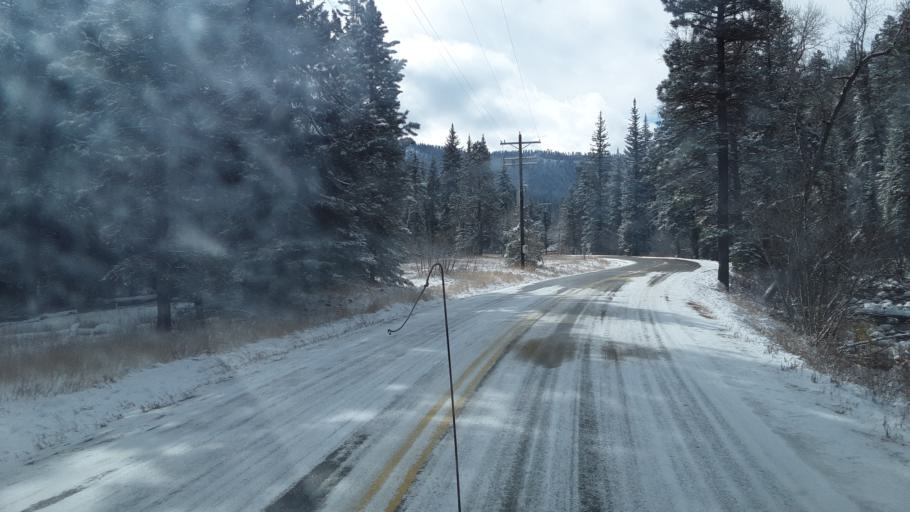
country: US
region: Colorado
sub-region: La Plata County
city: Bayfield
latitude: 37.3699
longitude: -107.6658
